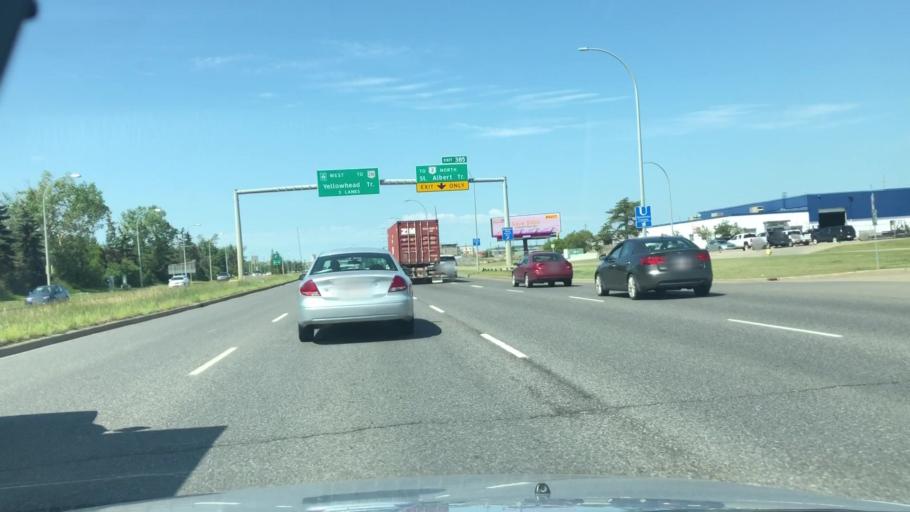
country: CA
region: Alberta
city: Edmonton
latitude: 53.5811
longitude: -113.5475
